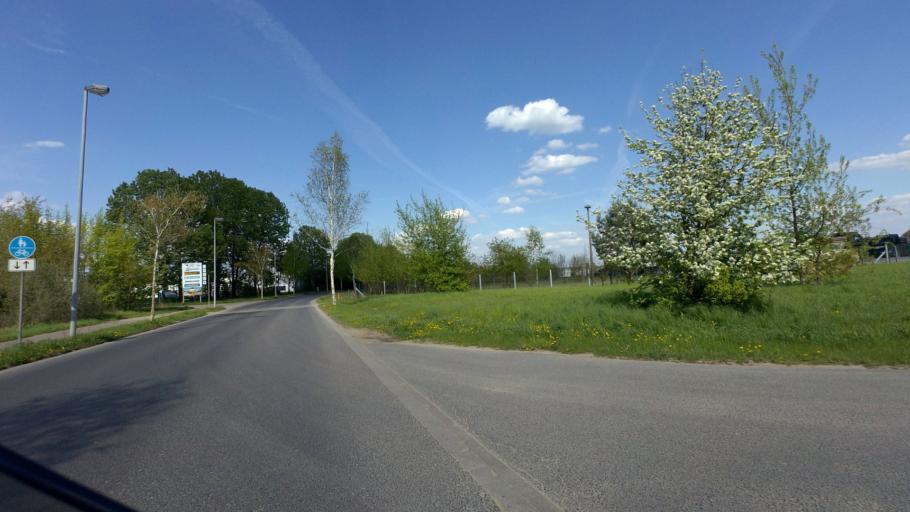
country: DE
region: Brandenburg
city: Templin
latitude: 53.1036
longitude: 13.4807
